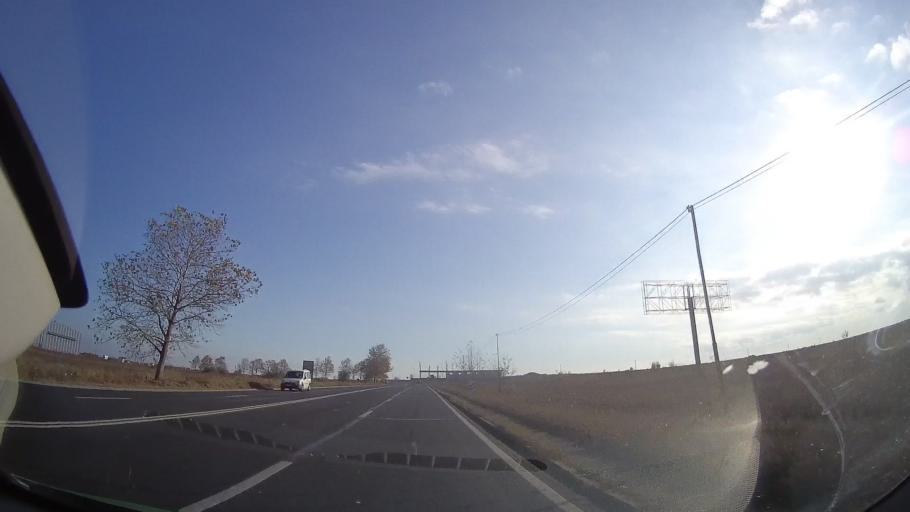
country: RO
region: Constanta
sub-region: Municipiul Mangalia
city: Mangalia
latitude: 43.7958
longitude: 28.5600
